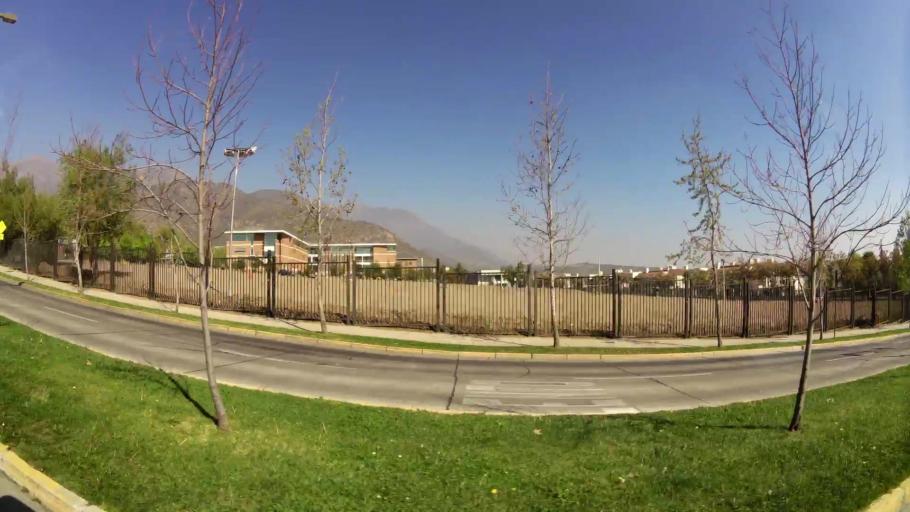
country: CL
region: Santiago Metropolitan
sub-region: Provincia de Santiago
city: Villa Presidente Frei, Nunoa, Santiago, Chile
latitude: -33.4012
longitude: -70.5092
